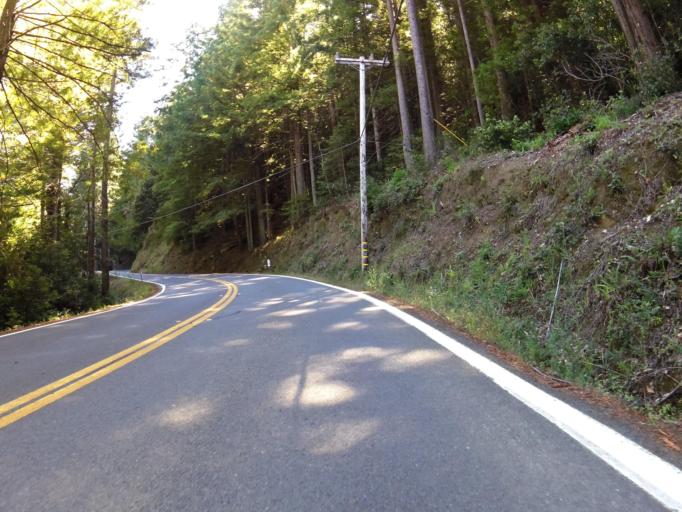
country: US
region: California
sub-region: Mendocino County
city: Fort Bragg
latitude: 39.7265
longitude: -123.8108
